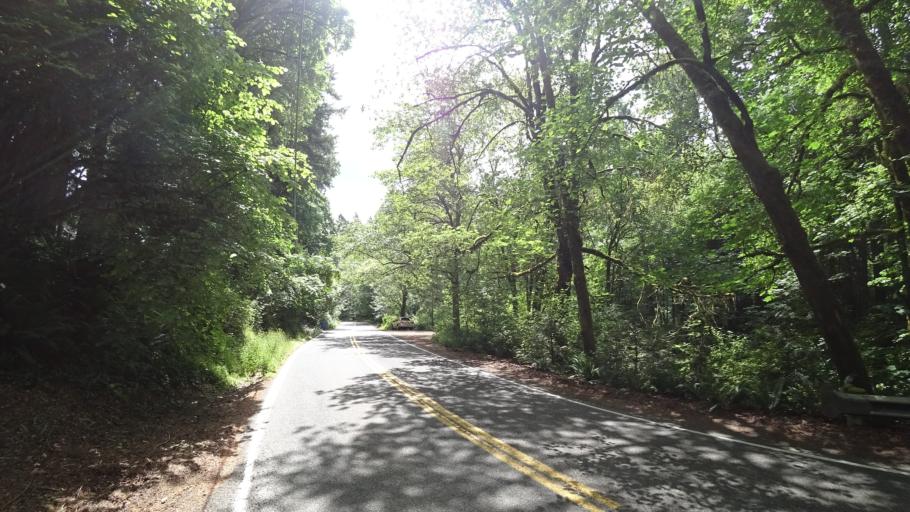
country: US
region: Oregon
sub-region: Clackamas County
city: Lake Oswego
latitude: 45.4460
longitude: -122.6929
